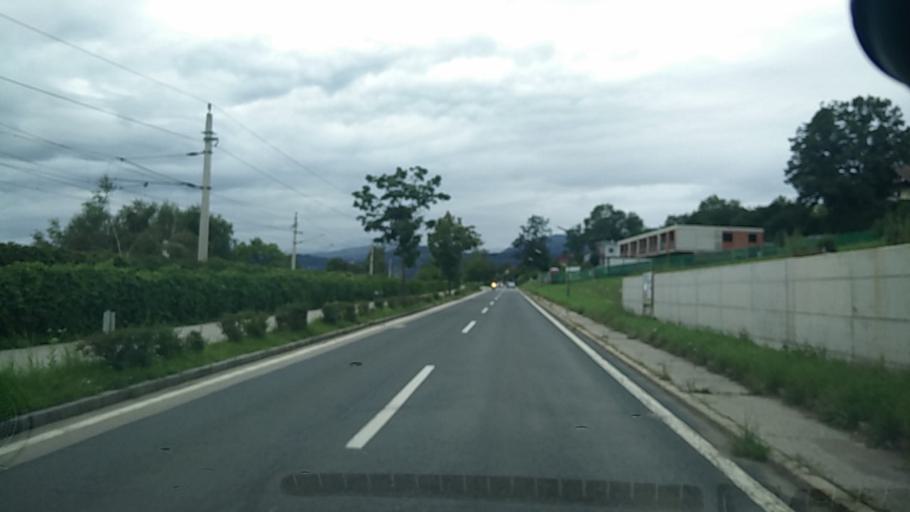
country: AT
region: Carinthia
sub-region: Politischer Bezirk Klagenfurt Land
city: Maria Worth
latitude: 46.6259
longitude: 14.1775
